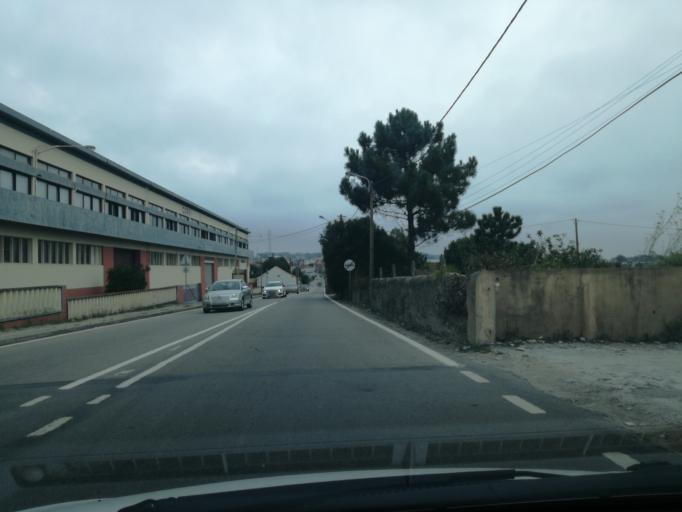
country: PT
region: Aveiro
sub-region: Espinho
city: Espinho
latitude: 41.0003
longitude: -8.6379
